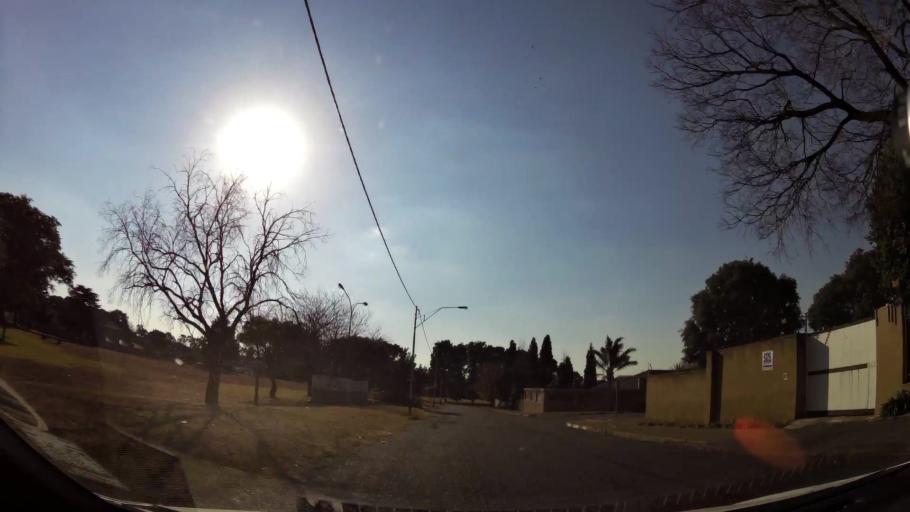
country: ZA
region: Gauteng
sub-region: City of Johannesburg Metropolitan Municipality
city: Johannesburg
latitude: -26.2430
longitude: 28.0163
